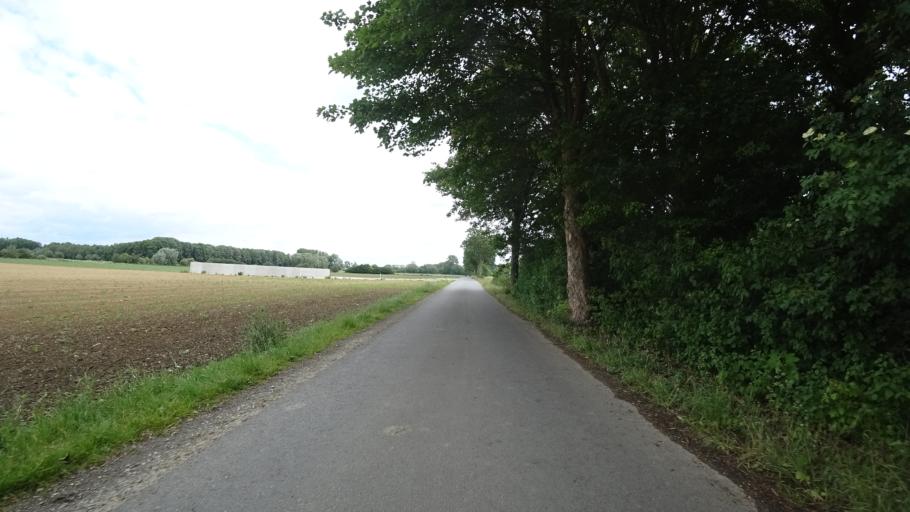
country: DE
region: North Rhine-Westphalia
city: Erwitte
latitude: 51.6279
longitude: 8.3810
